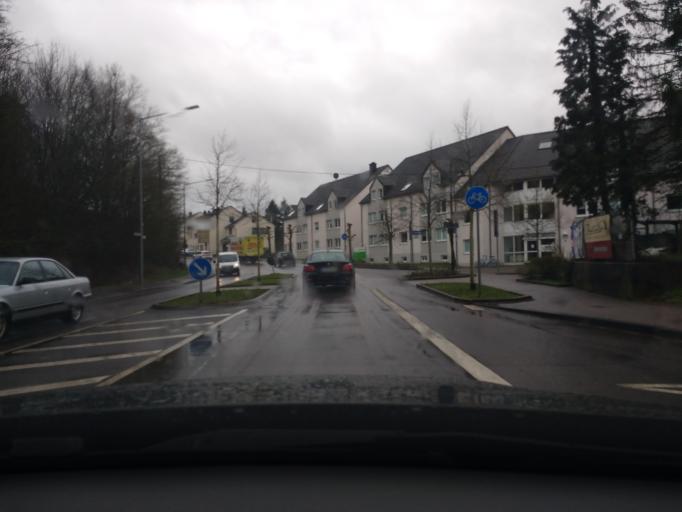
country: DE
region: Rheinland-Pfalz
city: Irsch
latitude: 49.7421
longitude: 6.6696
